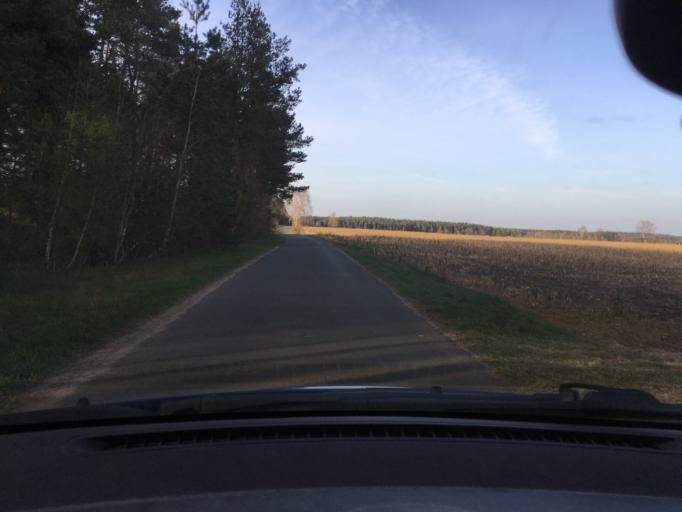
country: DE
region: Lower Saxony
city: Bispingen
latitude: 53.1087
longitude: 10.0112
